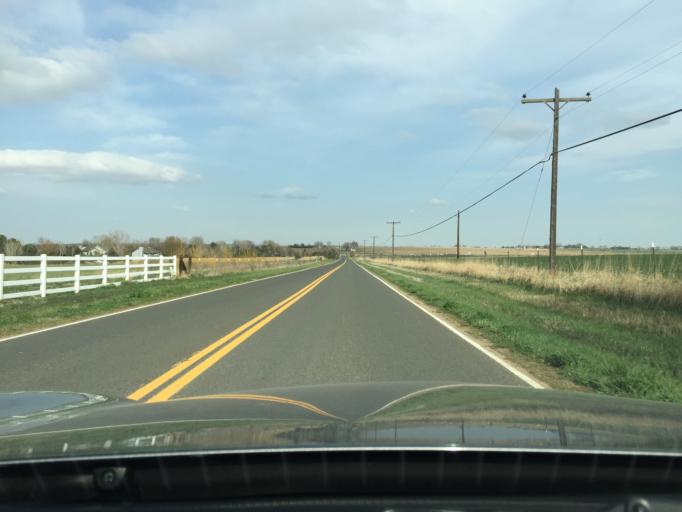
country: US
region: Colorado
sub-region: Boulder County
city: Longmont
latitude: 40.1162
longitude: -105.1149
